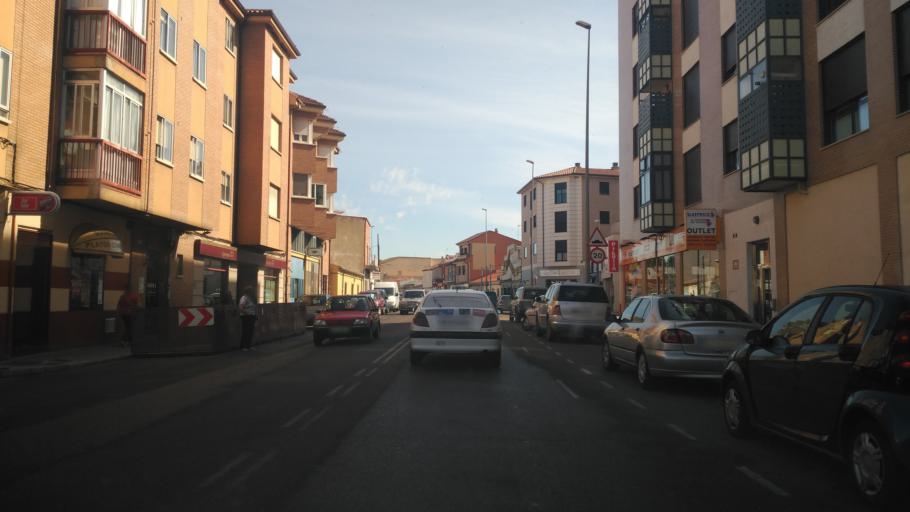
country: ES
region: Castille and Leon
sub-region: Provincia de Zamora
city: Zamora
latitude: 41.4963
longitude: -5.7405
